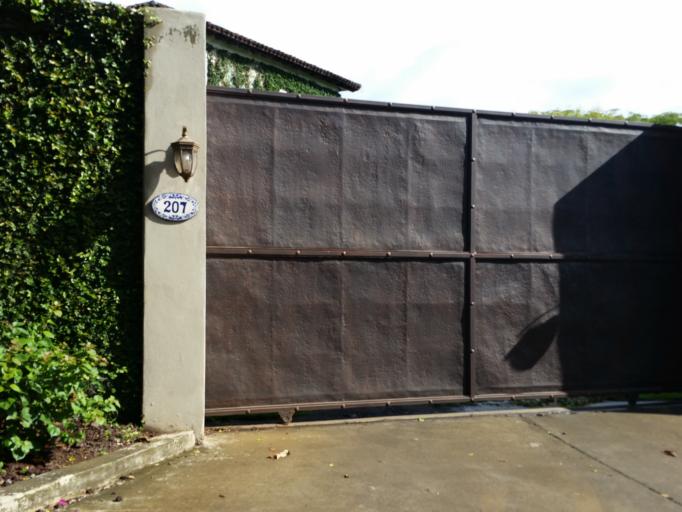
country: NI
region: Managua
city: Managua
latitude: 12.0933
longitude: -86.2575
